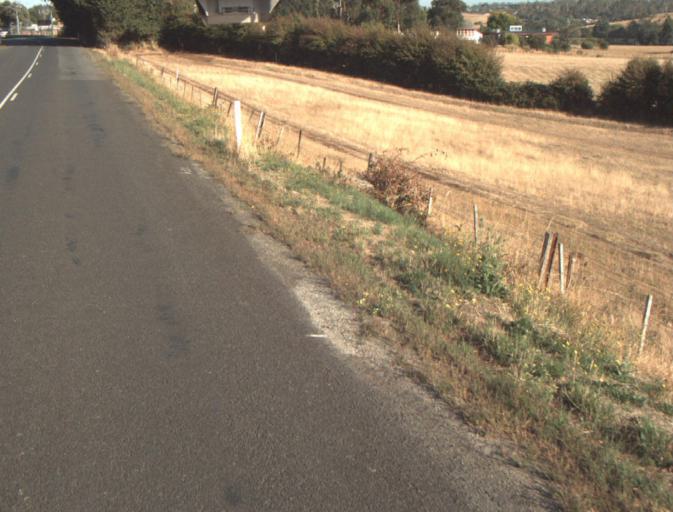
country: AU
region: Tasmania
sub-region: Launceston
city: Newstead
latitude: -41.4352
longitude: 147.1924
